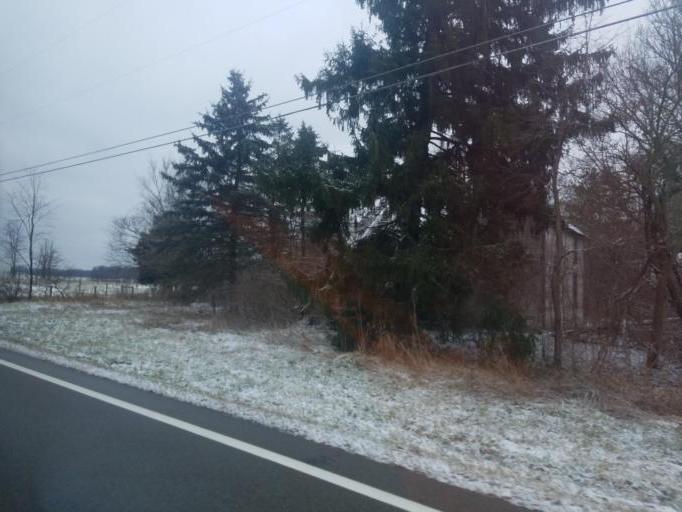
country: US
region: Ohio
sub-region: Licking County
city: Johnstown
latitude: 40.1756
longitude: -82.7279
